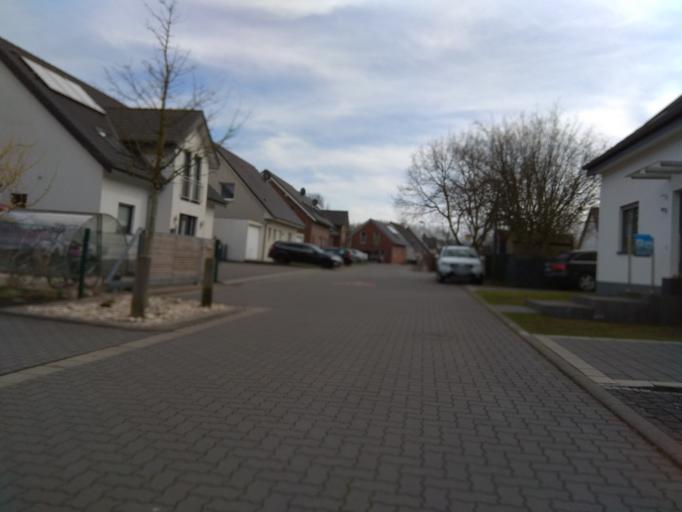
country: DE
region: North Rhine-Westphalia
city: Marl
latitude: 51.6421
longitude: 7.0814
